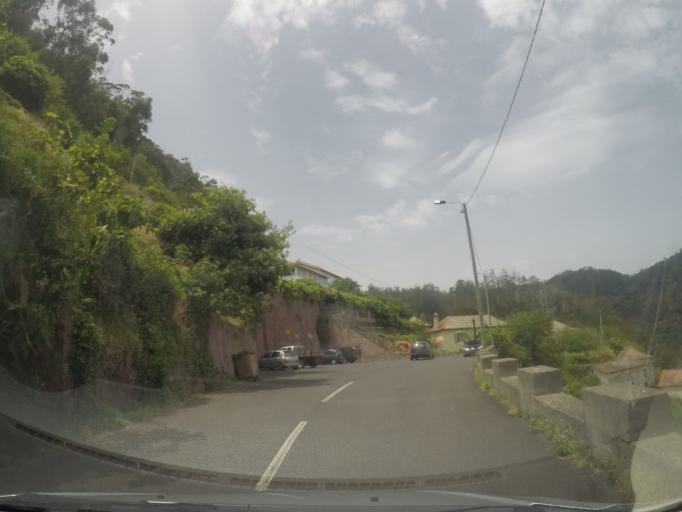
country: PT
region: Madeira
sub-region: Santa Cruz
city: Camacha
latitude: 32.6786
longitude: -16.8386
